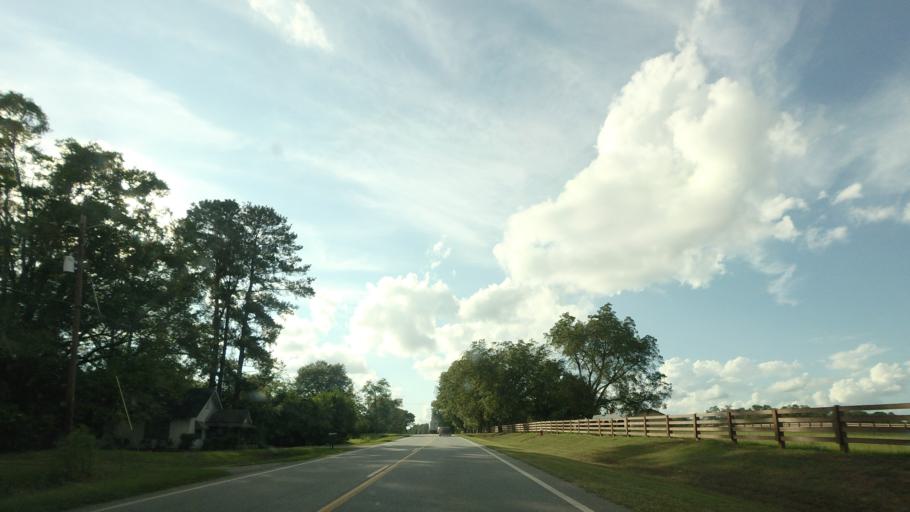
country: US
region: Georgia
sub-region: Pulaski County
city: Hawkinsville
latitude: 32.2870
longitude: -83.4867
